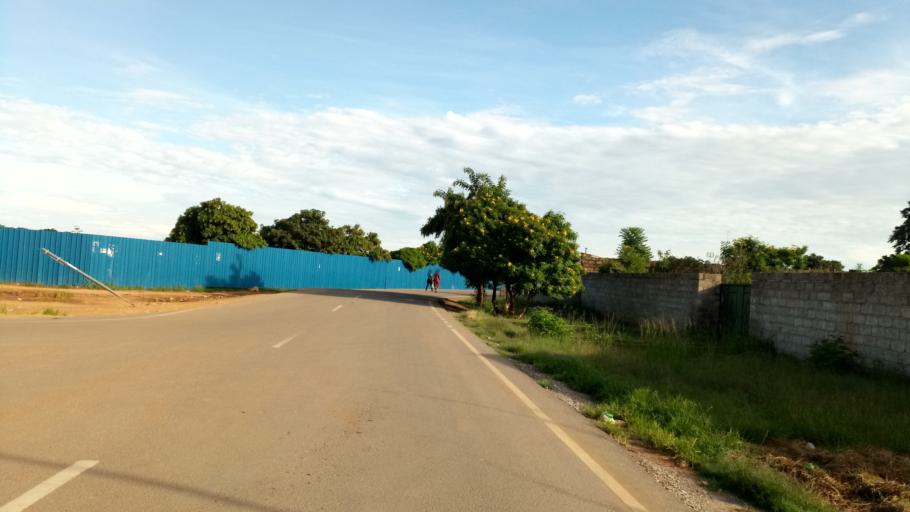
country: ZM
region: Lusaka
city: Lusaka
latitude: -15.4461
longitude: 28.3188
